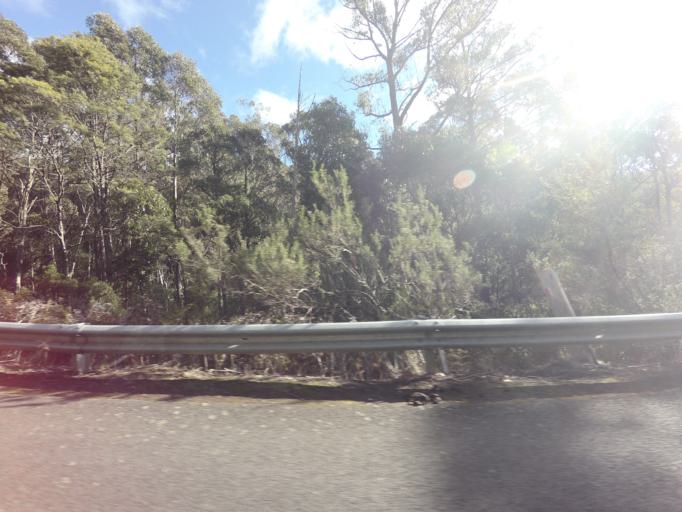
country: AU
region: Tasmania
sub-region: Glenorchy
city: Berriedale
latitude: -42.8384
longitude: 147.1658
